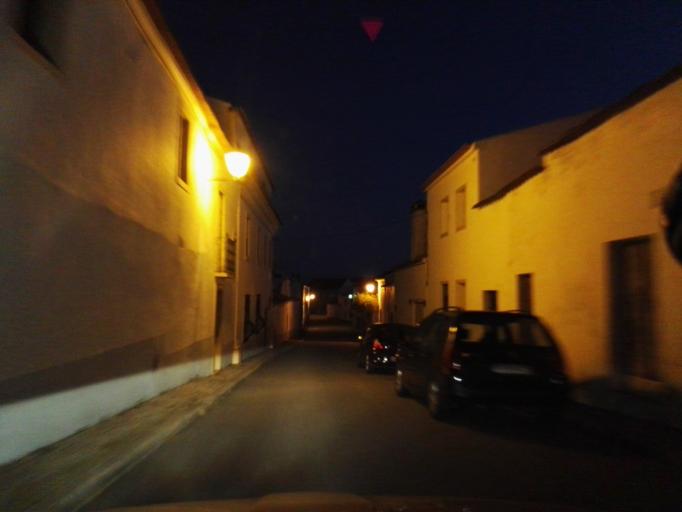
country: PT
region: Evora
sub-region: Arraiolos
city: Arraiolos
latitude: 38.8311
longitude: -7.8369
